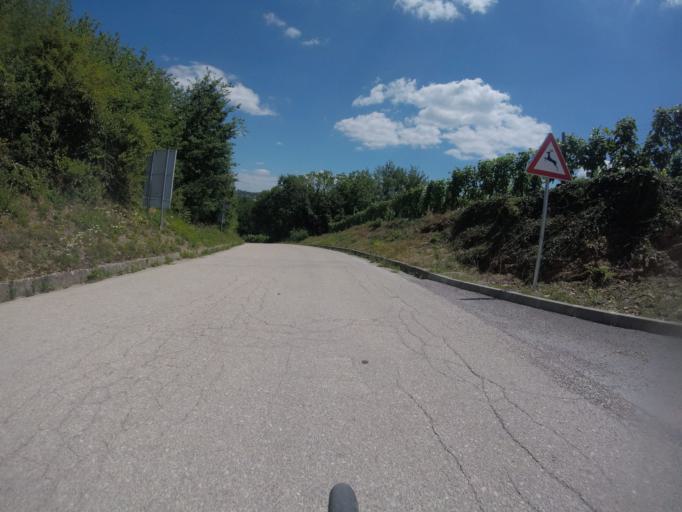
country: HR
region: Karlovacka
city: Ozalj
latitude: 45.6734
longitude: 15.4049
